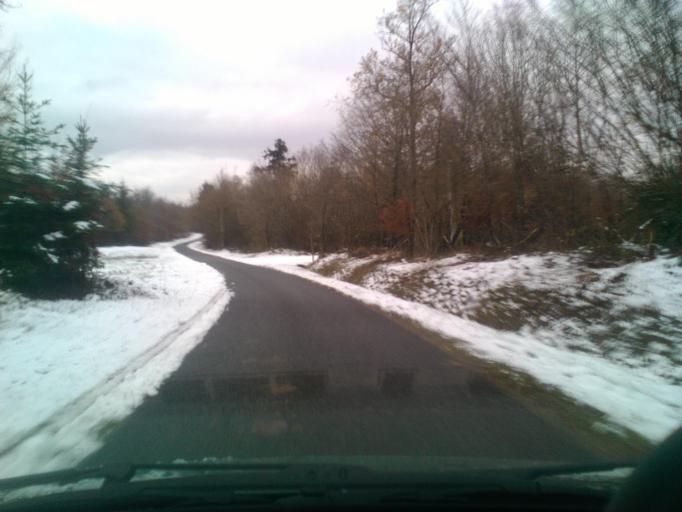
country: FR
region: Lorraine
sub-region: Departement des Vosges
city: Sainte-Marguerite
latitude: 48.2910
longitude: 7.0246
